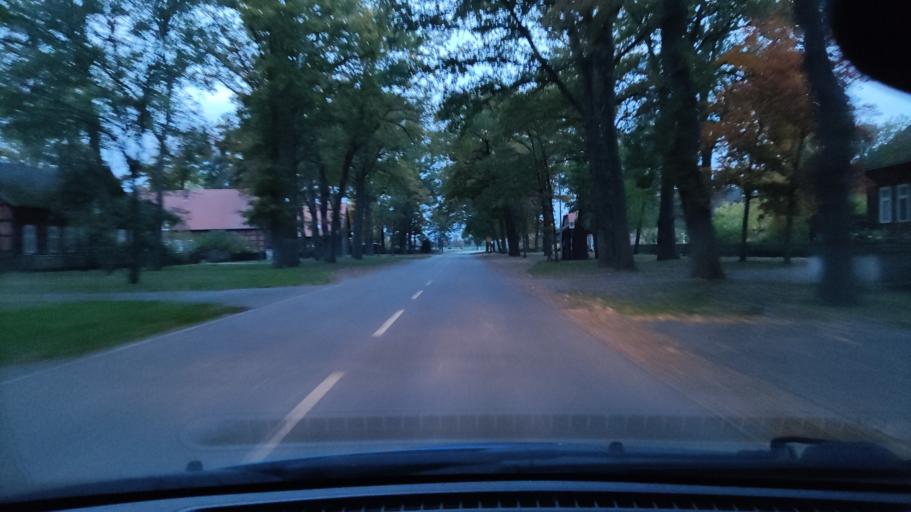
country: DE
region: Lower Saxony
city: Trebel
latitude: 52.9643
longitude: 11.3008
